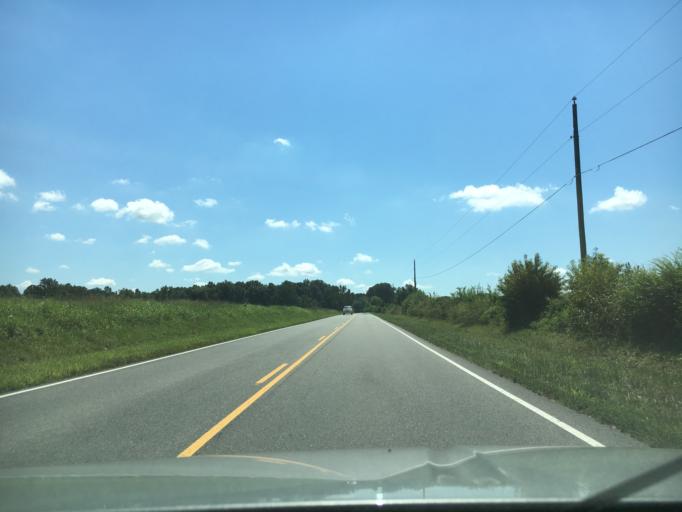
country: US
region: Virginia
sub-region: Amelia County
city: Amelia Court House
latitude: 37.3979
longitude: -77.8995
